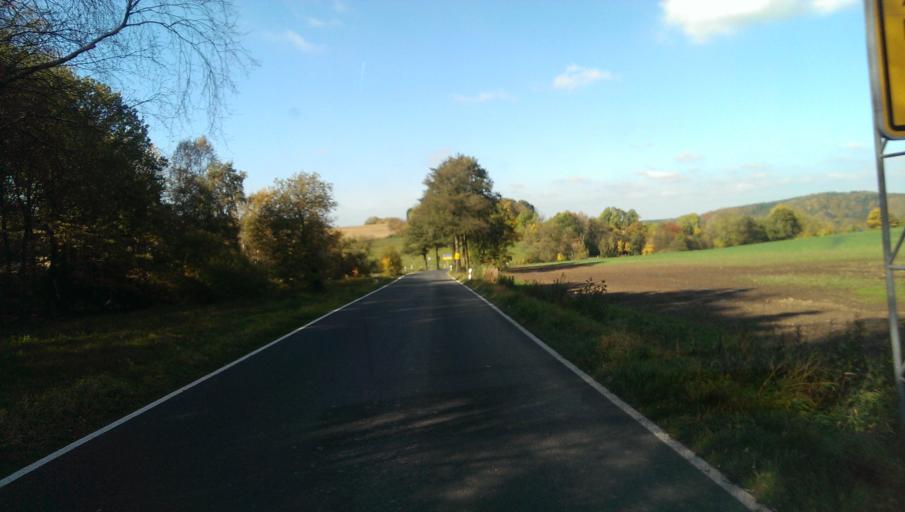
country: DE
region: Saxony
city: Dohma
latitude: 50.8319
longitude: 13.9478
